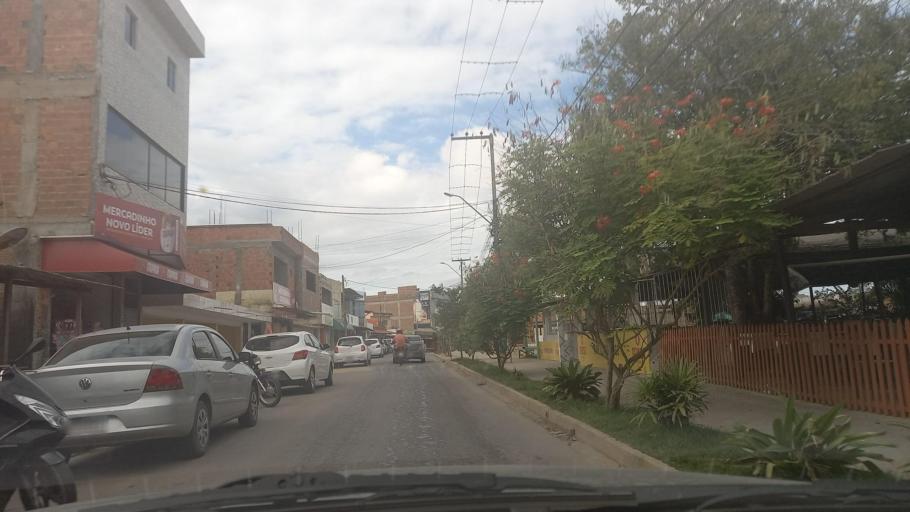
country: BR
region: Pernambuco
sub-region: Caruaru
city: Caruaru
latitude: -8.2910
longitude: -36.0295
